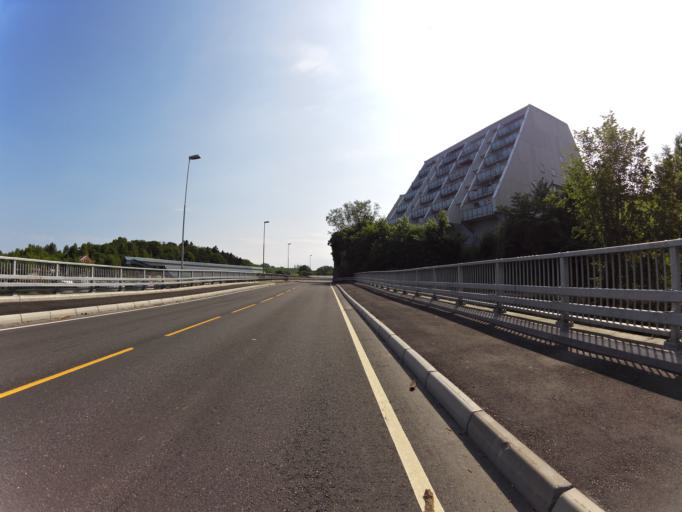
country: NO
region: Ostfold
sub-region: Sarpsborg
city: Sarpsborg
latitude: 59.2707
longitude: 11.0896
